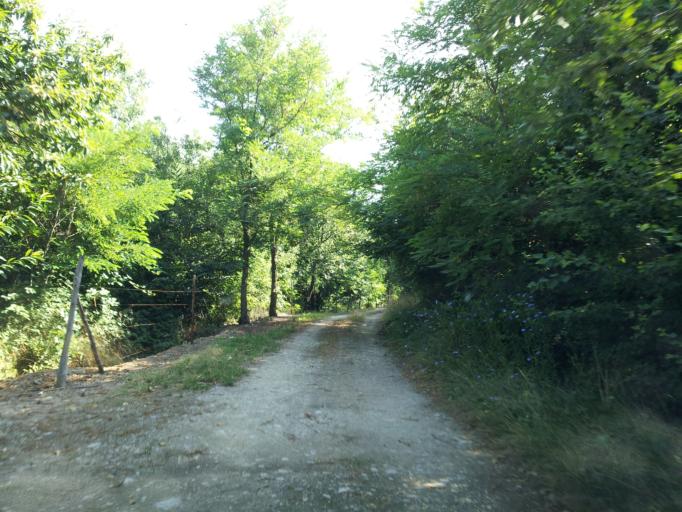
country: HU
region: Zala
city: Cserszegtomaj
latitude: 46.8492
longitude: 17.2187
